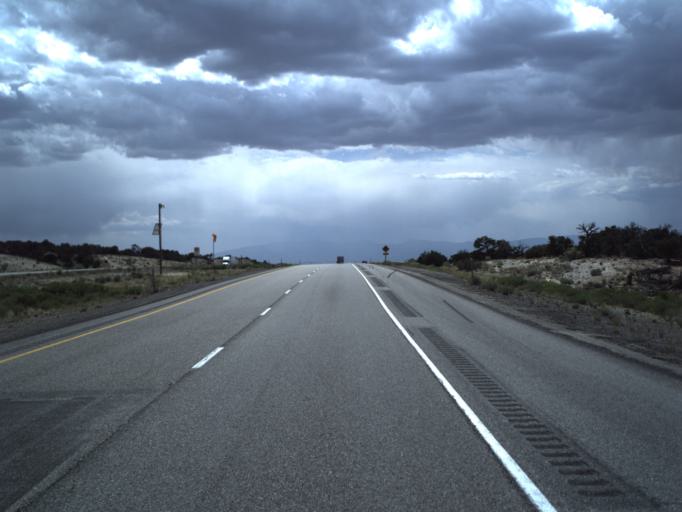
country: US
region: Utah
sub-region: Emery County
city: Ferron
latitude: 38.8522
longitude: -110.9260
